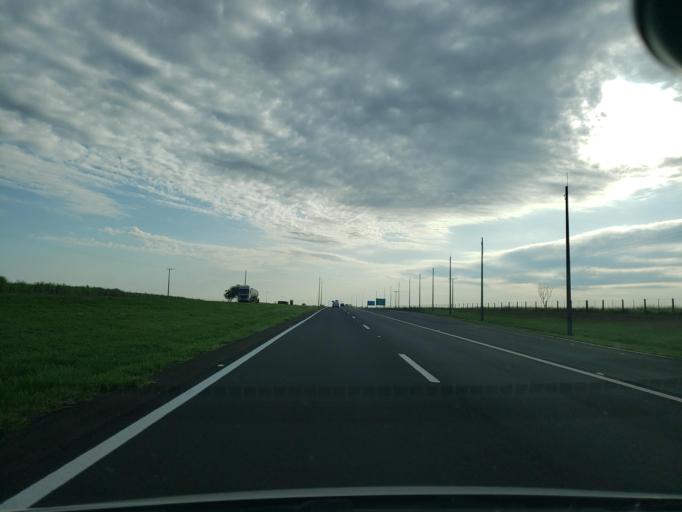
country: BR
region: Sao Paulo
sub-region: Guararapes
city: Guararapes
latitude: -21.2123
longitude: -50.7143
